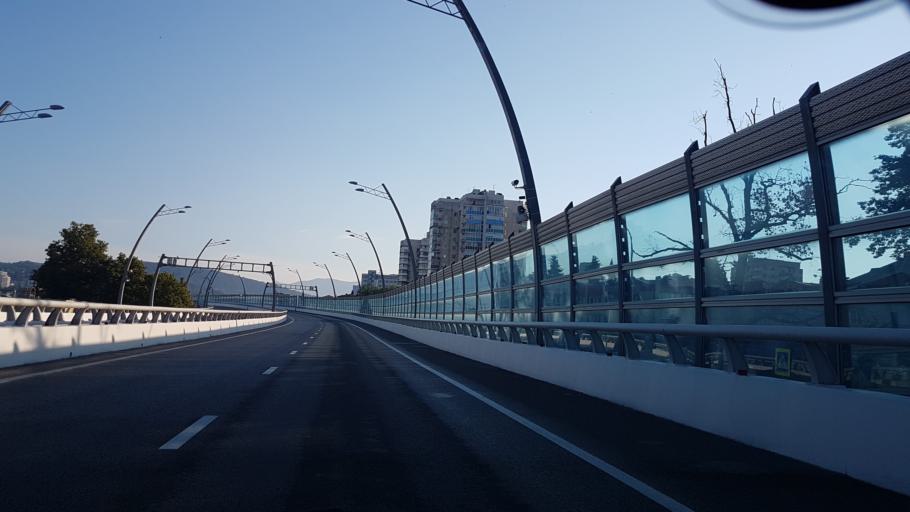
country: RU
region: Krasnodarskiy
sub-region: Sochi City
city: Sochi
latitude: 43.5939
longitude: 39.7313
